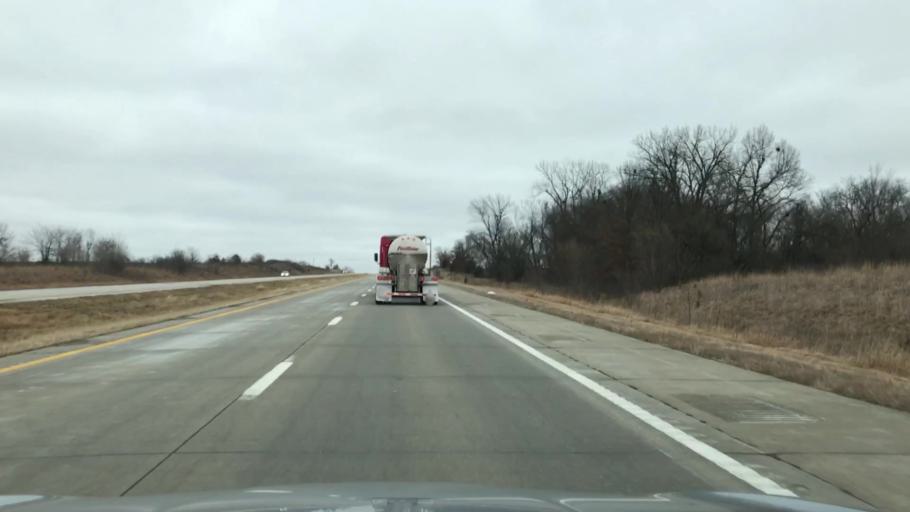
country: US
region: Missouri
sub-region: Caldwell County
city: Hamilton
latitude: 39.7351
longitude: -93.9378
